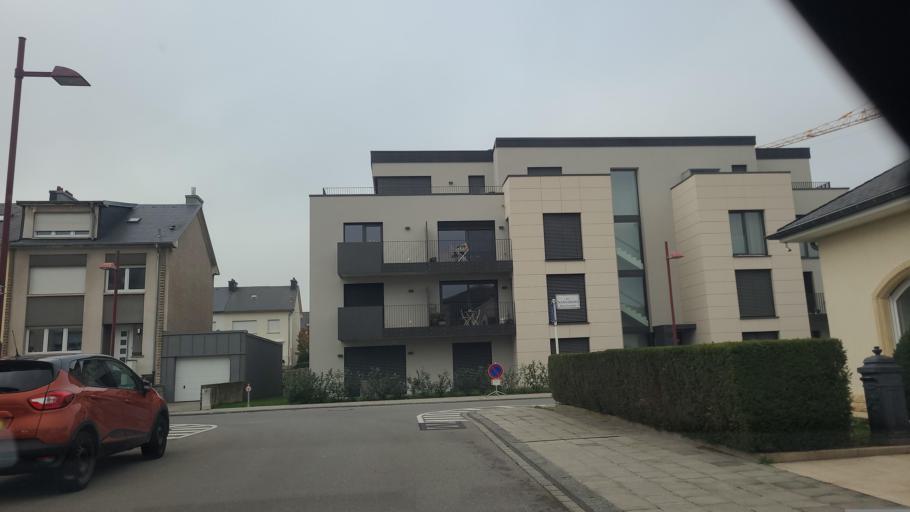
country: LU
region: Luxembourg
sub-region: Canton d'Esch-sur-Alzette
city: Petange
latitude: 49.5593
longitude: 5.8827
